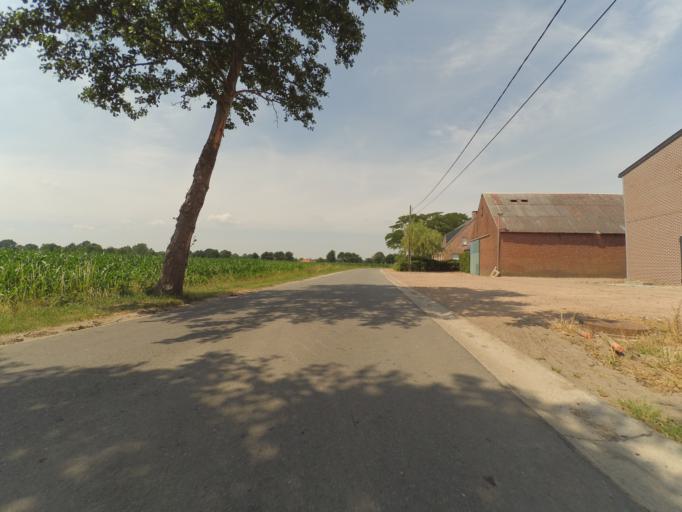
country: BE
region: Flanders
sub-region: Provincie Antwerpen
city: Wuustwezel
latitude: 51.4118
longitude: 4.5952
